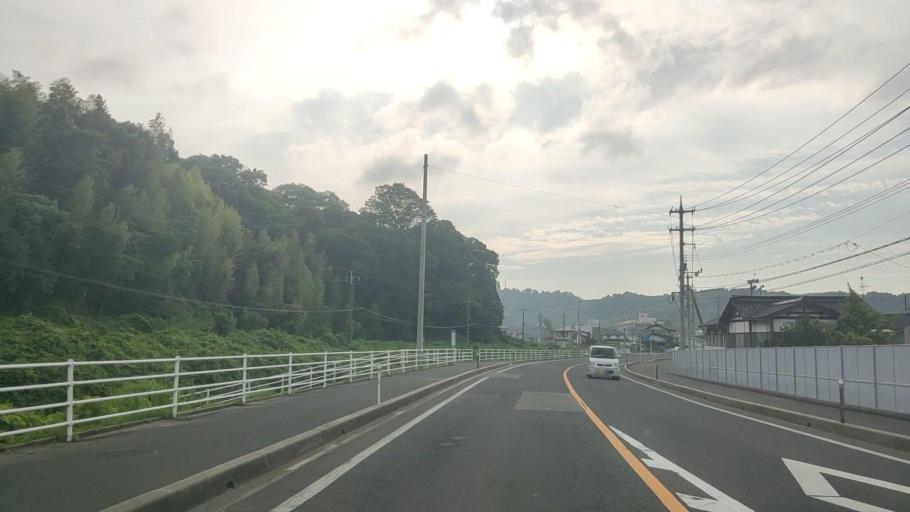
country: JP
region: Tottori
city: Kurayoshi
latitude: 35.4582
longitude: 133.8383
